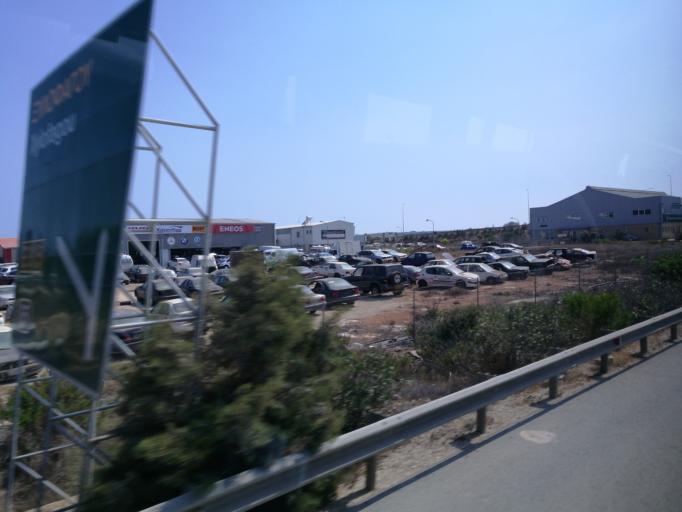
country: CY
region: Ammochostos
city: Liopetri
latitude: 34.9684
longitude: 33.8667
